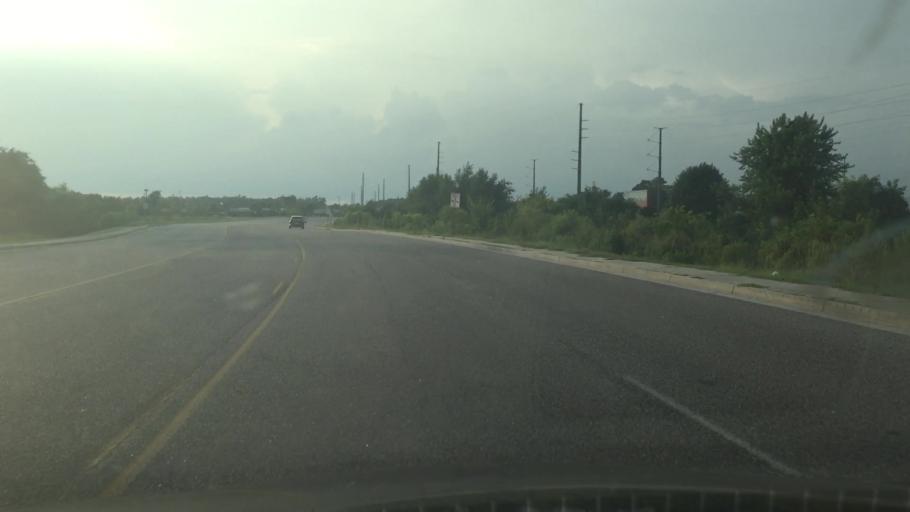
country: US
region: South Carolina
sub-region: Horry County
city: Forestbrook
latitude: 33.7140
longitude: -78.9282
